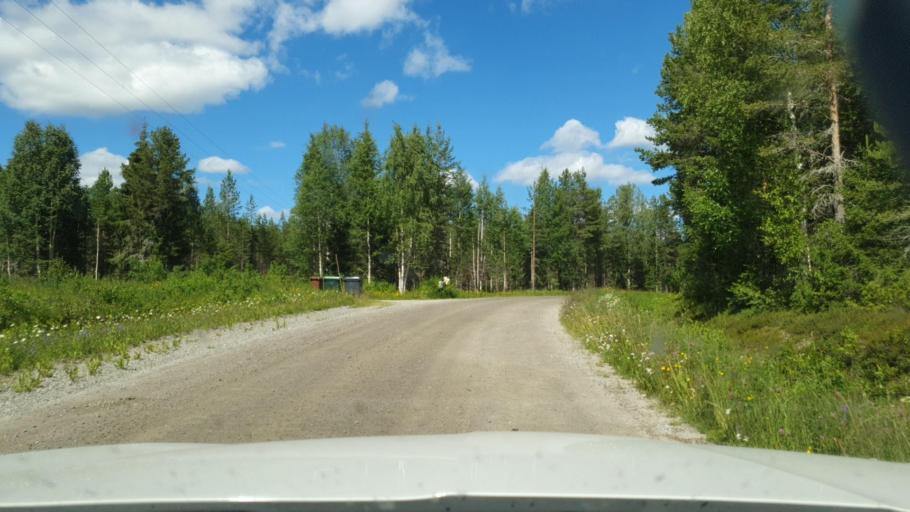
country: SE
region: Vaesterbotten
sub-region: Skelleftea Kommun
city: Backa
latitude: 65.1527
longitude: 21.1608
